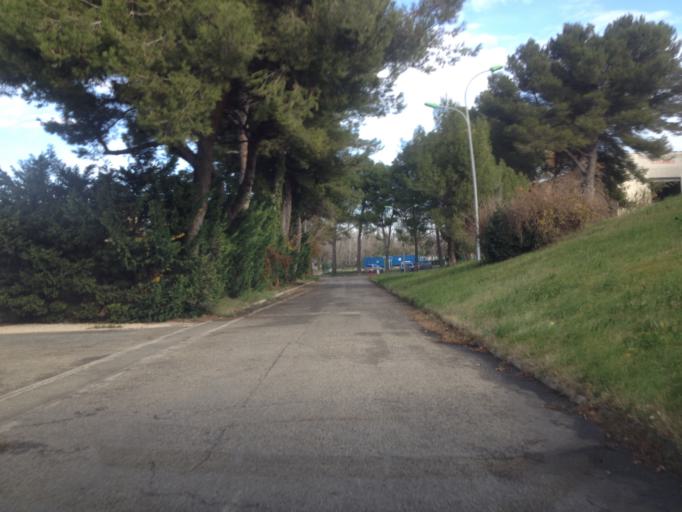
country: FR
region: Provence-Alpes-Cote d'Azur
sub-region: Departement du Vaucluse
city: Bedarrides
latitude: 44.0374
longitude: 4.8904
